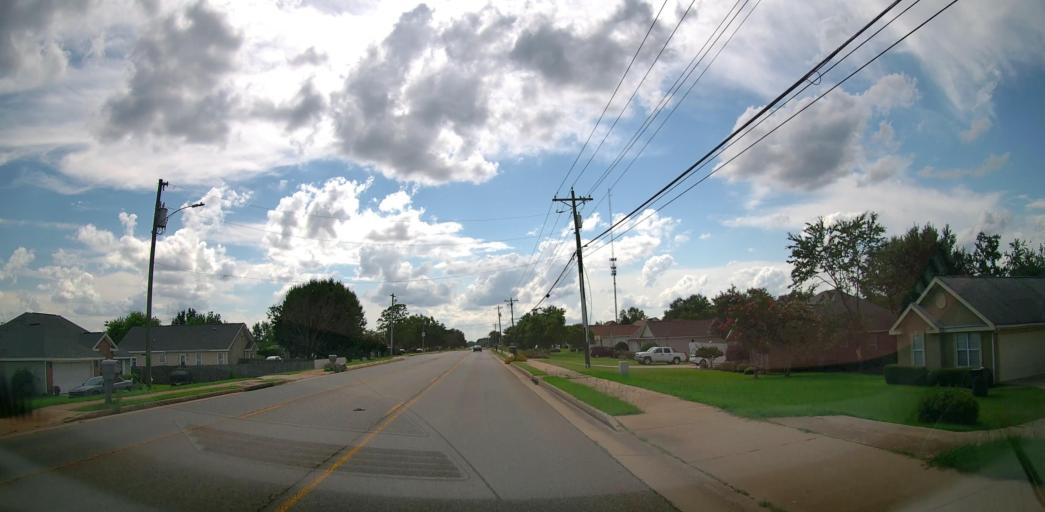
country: US
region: Georgia
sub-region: Houston County
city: Centerville
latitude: 32.5709
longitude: -83.6661
